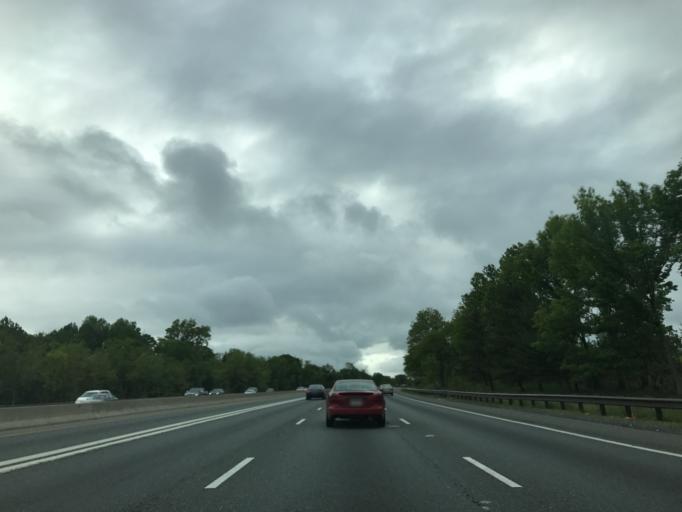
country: US
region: Maryland
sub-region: Prince George's County
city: Woodmore
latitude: 38.9438
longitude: -76.7908
